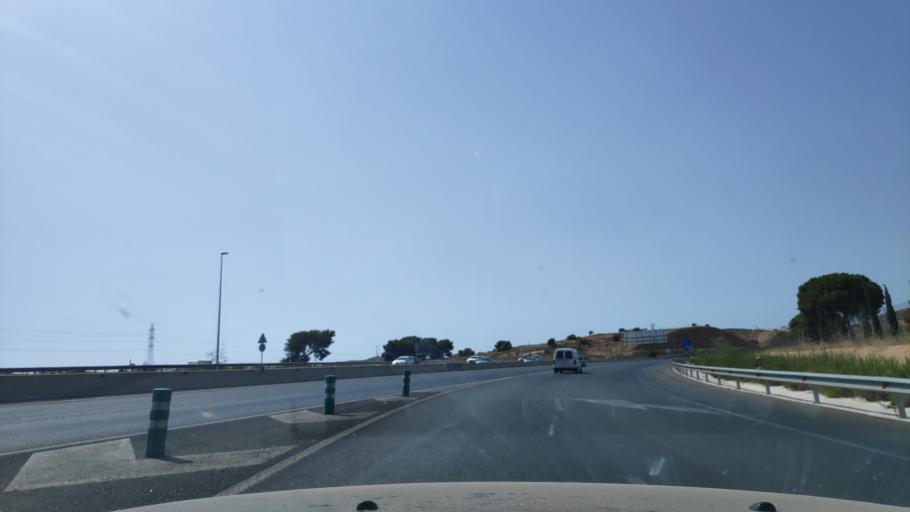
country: ES
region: Murcia
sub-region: Murcia
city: Murcia
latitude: 38.0320
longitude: -1.1569
